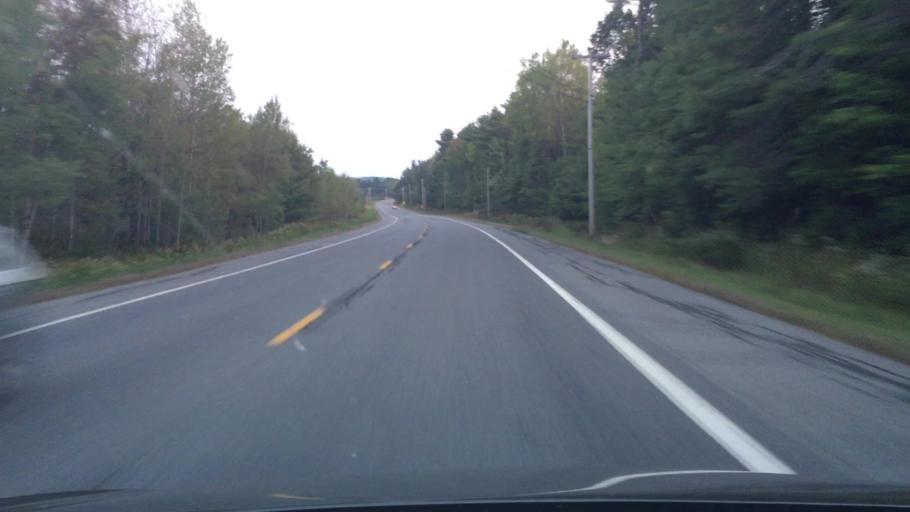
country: US
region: Maine
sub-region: Waldo County
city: Stockton Springs
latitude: 44.5448
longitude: -68.8637
